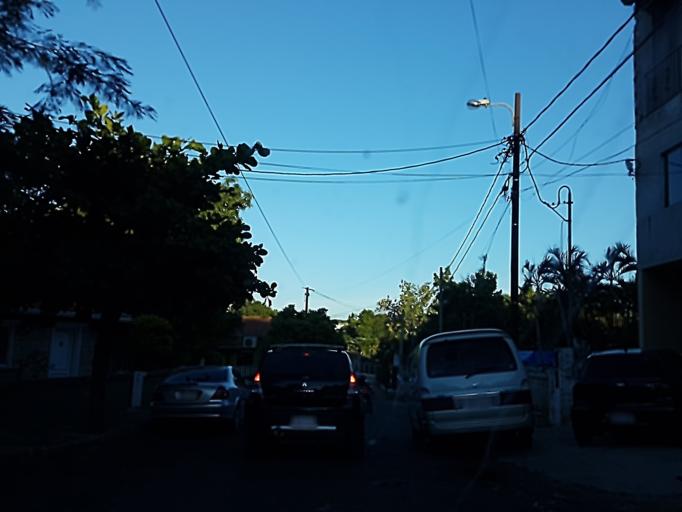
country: PY
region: Asuncion
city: Asuncion
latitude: -25.2691
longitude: -57.5905
